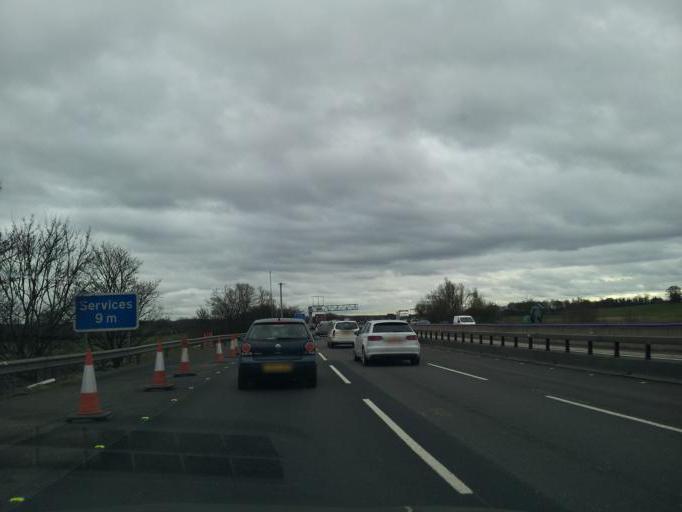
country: GB
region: England
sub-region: Staffordshire
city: Penkridge
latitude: 52.7598
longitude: -2.1031
